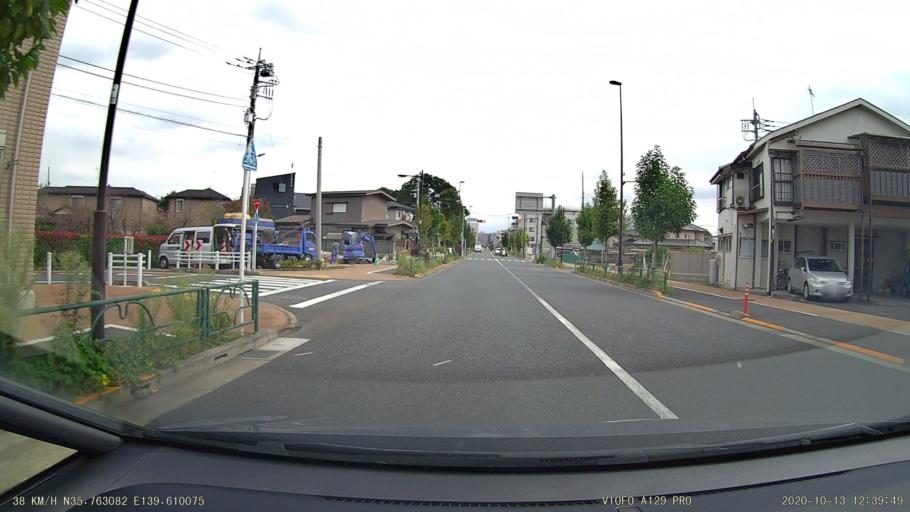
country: JP
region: Saitama
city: Wako
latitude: 35.7630
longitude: 139.6101
